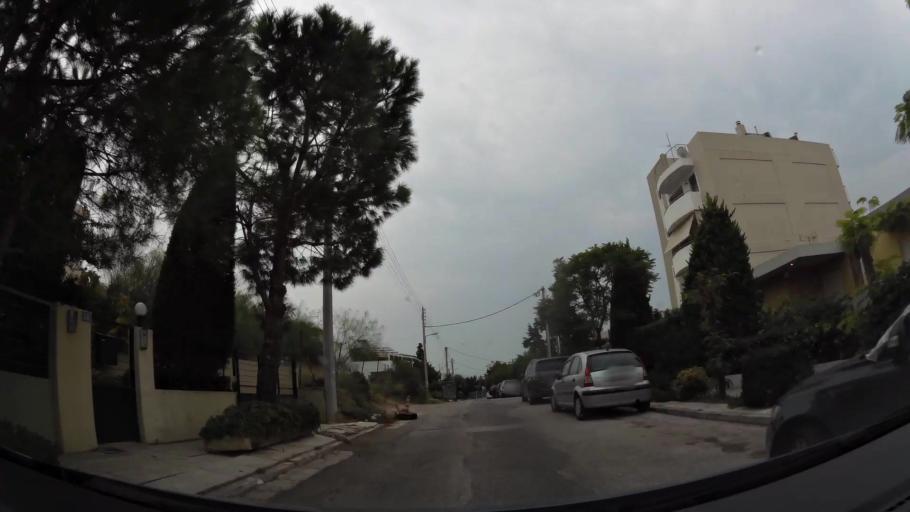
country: GR
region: Attica
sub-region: Nomarchia Athinas
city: Alimos
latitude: 37.9103
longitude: 23.7213
